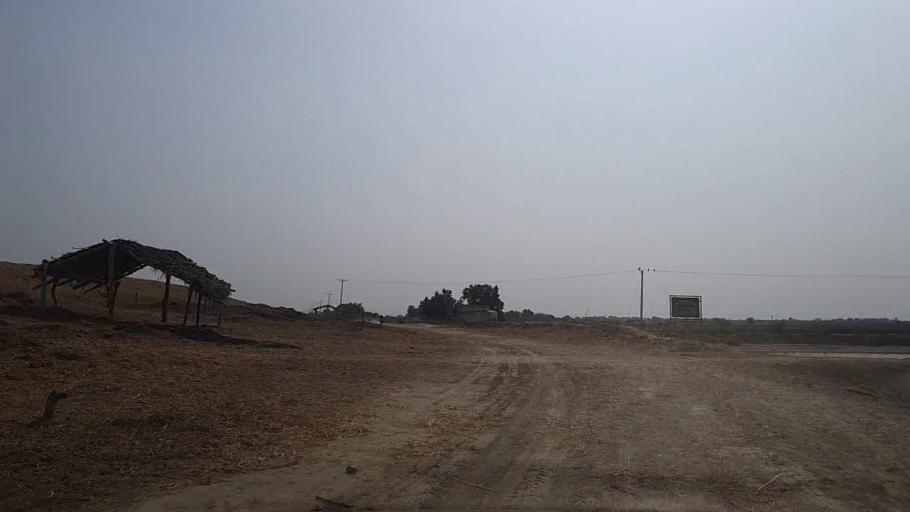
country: PK
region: Sindh
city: Thatta
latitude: 24.5632
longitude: 67.9132
